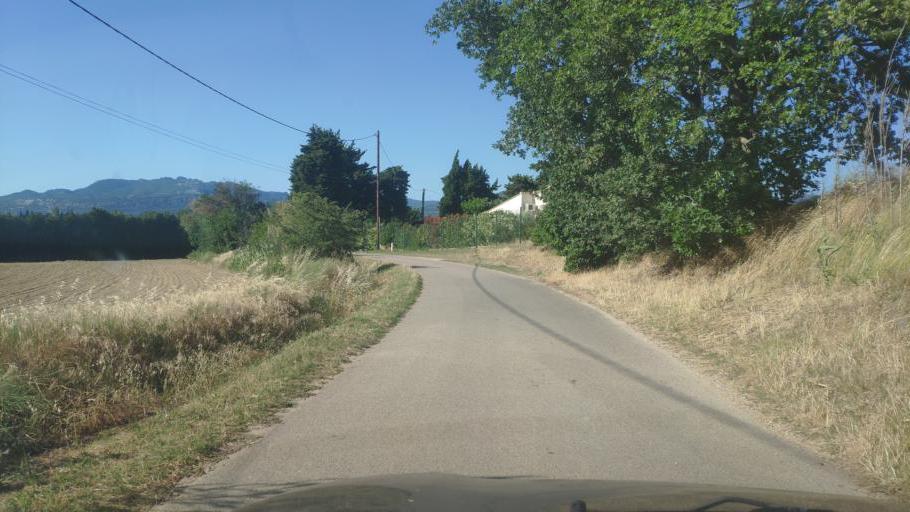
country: FR
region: Provence-Alpes-Cote d'Azur
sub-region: Departement du Vaucluse
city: Loriol-du-Comtat
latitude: 44.0761
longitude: 5.0186
